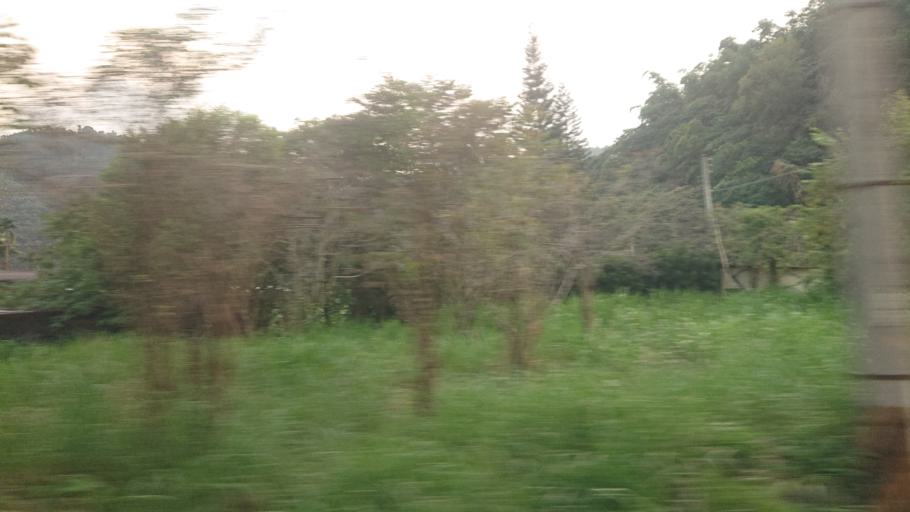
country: TW
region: Taiwan
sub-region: Nantou
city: Puli
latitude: 23.9702
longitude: 120.9970
